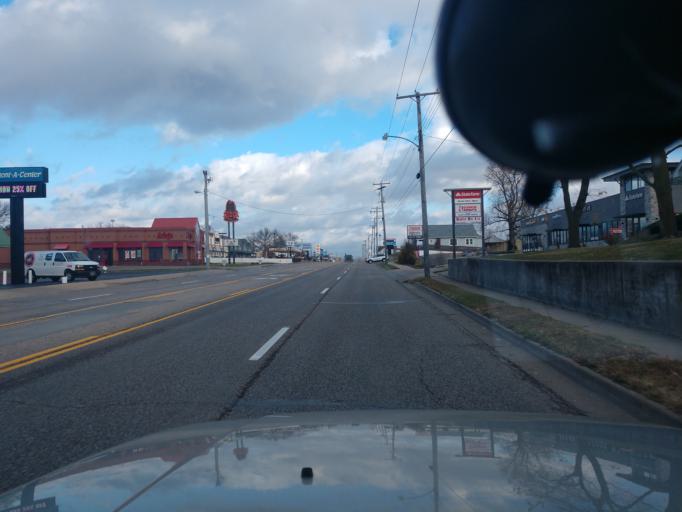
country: US
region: Illinois
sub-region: Adams County
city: Quincy
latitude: 39.9353
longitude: -91.3741
